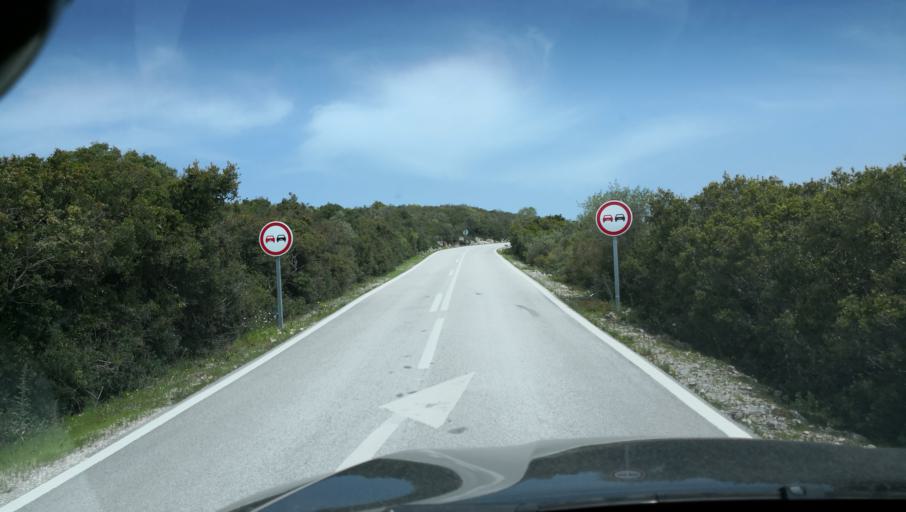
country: PT
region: Setubal
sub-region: Palmela
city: Quinta do Anjo
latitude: 38.4860
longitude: -8.9878
